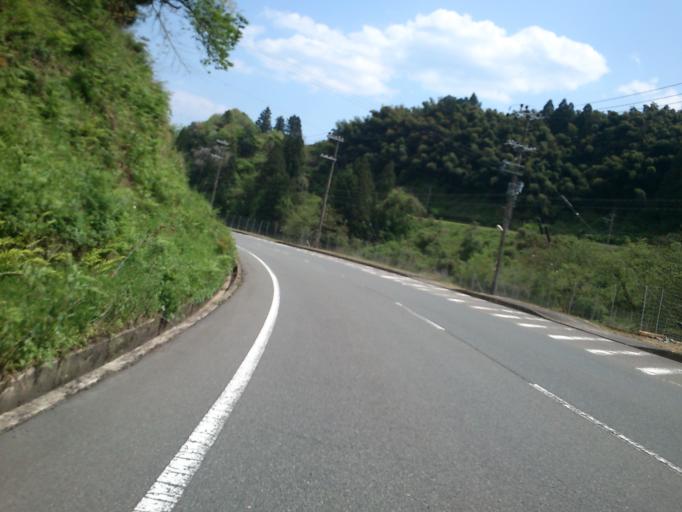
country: JP
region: Kyoto
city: Fukuchiyama
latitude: 35.3381
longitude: 134.9387
